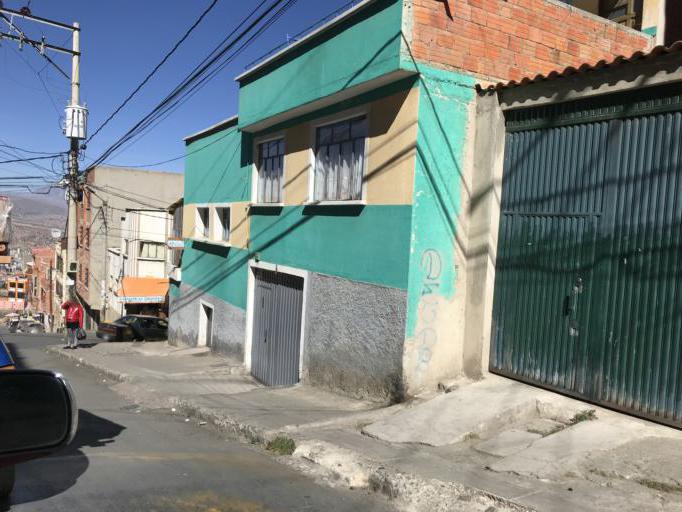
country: BO
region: La Paz
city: La Paz
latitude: -16.4881
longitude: -68.1616
